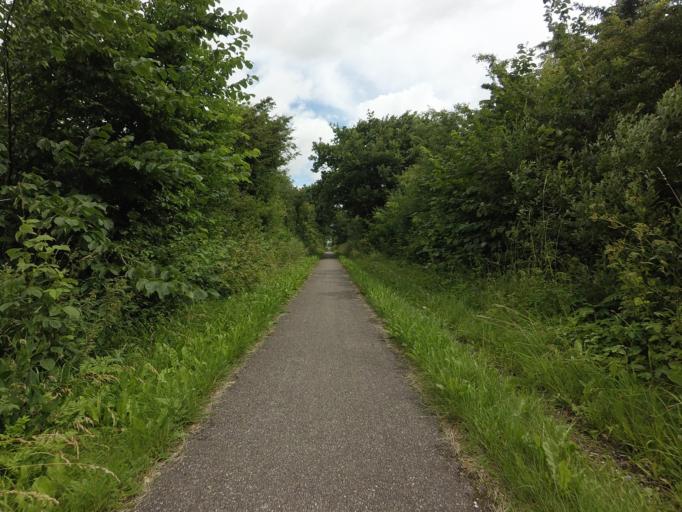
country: DK
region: Central Jutland
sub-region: Favrskov Kommune
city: Hammel
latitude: 56.3095
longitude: 9.8441
